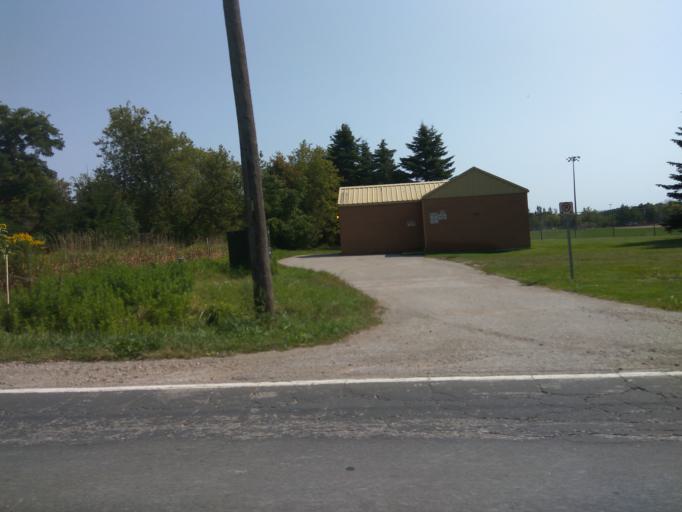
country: CA
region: Ontario
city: Stratford
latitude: 43.3875
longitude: -80.9989
